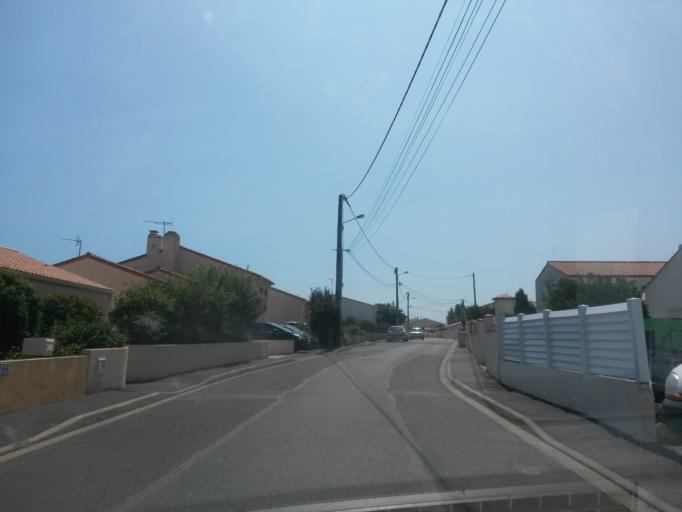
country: FR
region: Pays de la Loire
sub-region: Departement de la Vendee
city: Les Sables-d'Olonne
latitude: 46.5108
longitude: -1.8076
